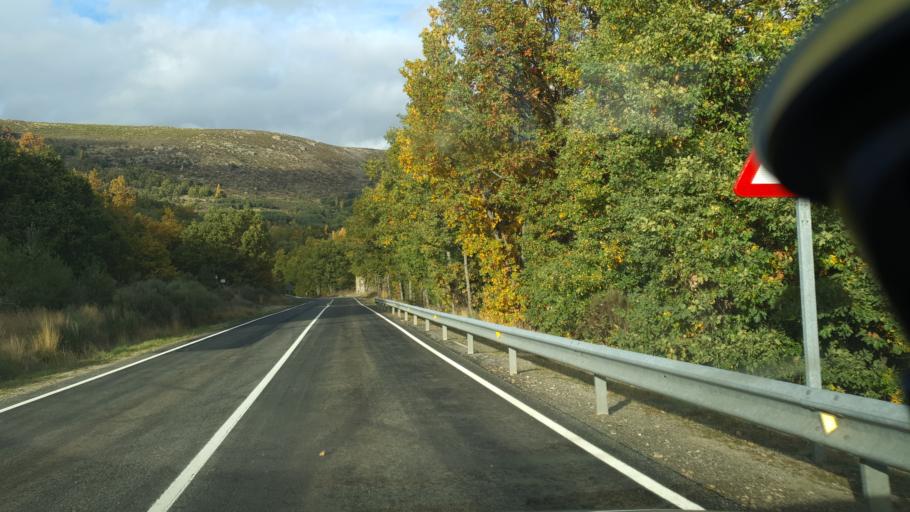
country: ES
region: Castille and Leon
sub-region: Provincia de Avila
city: Hoyocasero
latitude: 40.3963
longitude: -4.9868
